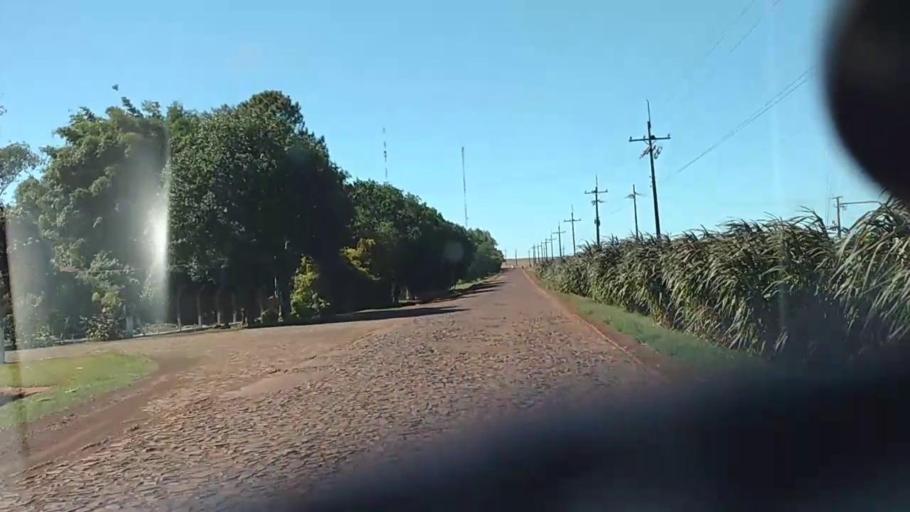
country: PY
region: Alto Parana
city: Naranjal
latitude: -25.9767
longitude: -55.1661
